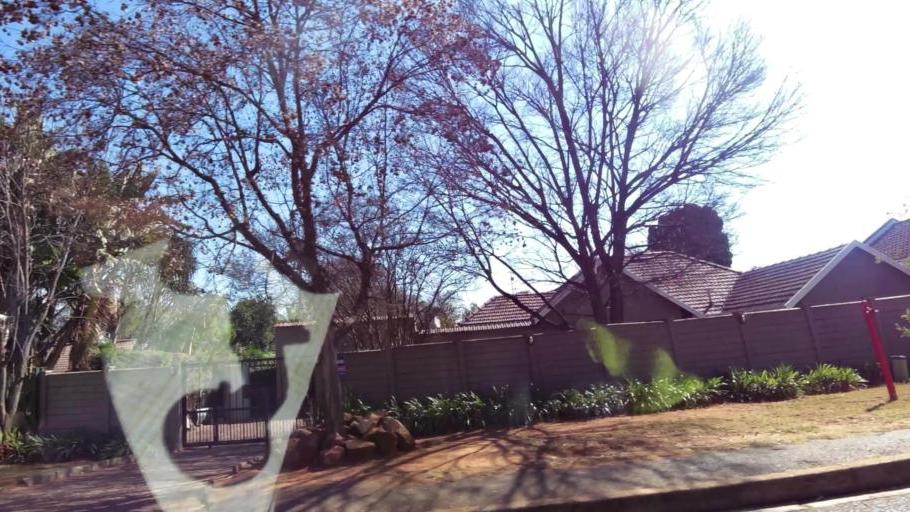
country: ZA
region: Gauteng
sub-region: City of Johannesburg Metropolitan Municipality
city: Roodepoort
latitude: -26.1327
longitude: 27.9584
